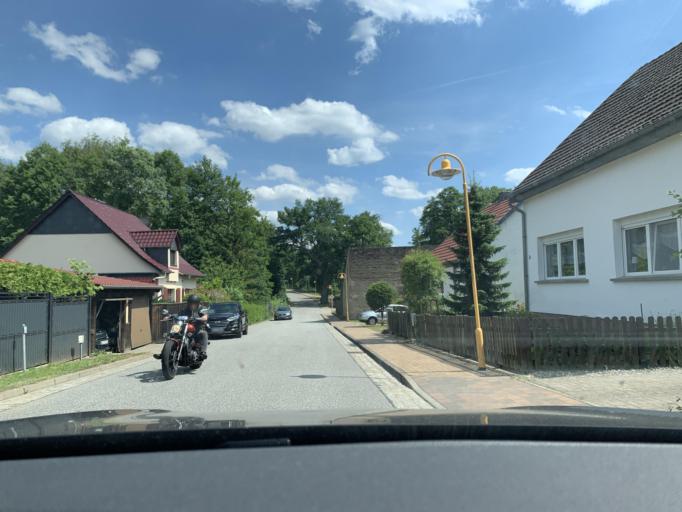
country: DE
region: Brandenburg
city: Rheinsberg
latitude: 53.1570
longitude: 12.8692
